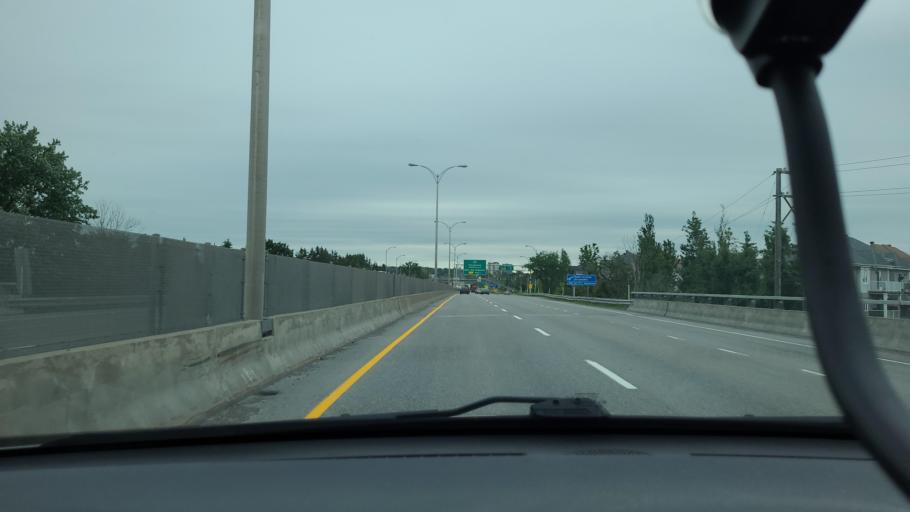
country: CA
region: Quebec
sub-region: Lanaudiere
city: Terrebonne
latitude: 45.6887
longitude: -73.6503
